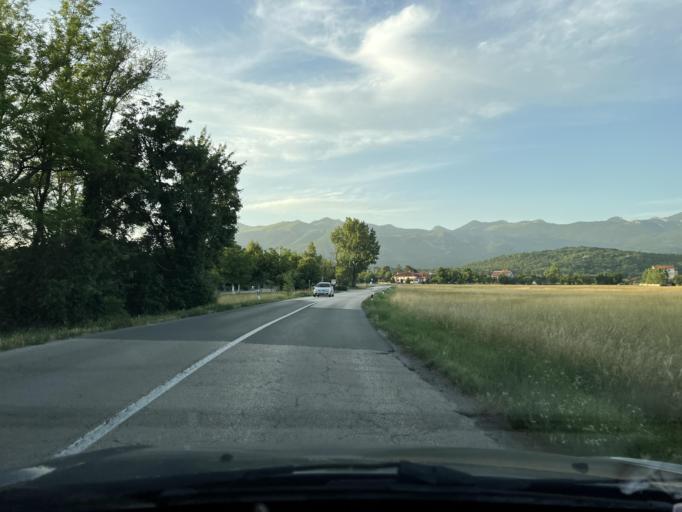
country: HR
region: Primorsko-Goranska
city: Drazice
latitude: 45.3818
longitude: 14.4700
